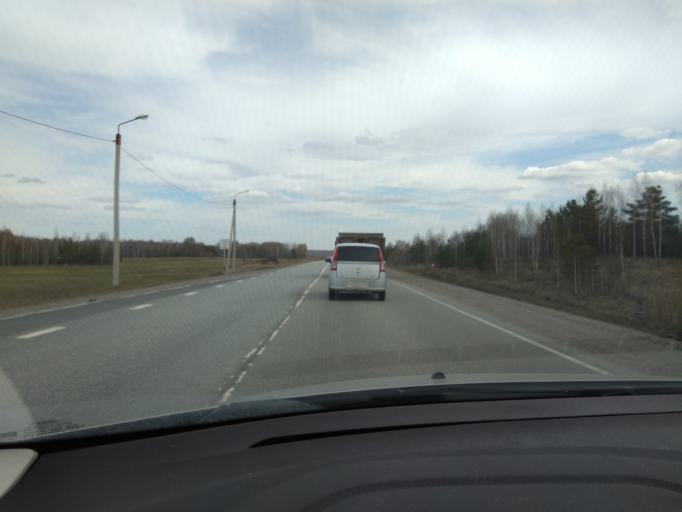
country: RU
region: Sverdlovsk
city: Yelanskiy
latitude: 56.7586
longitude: 62.3464
